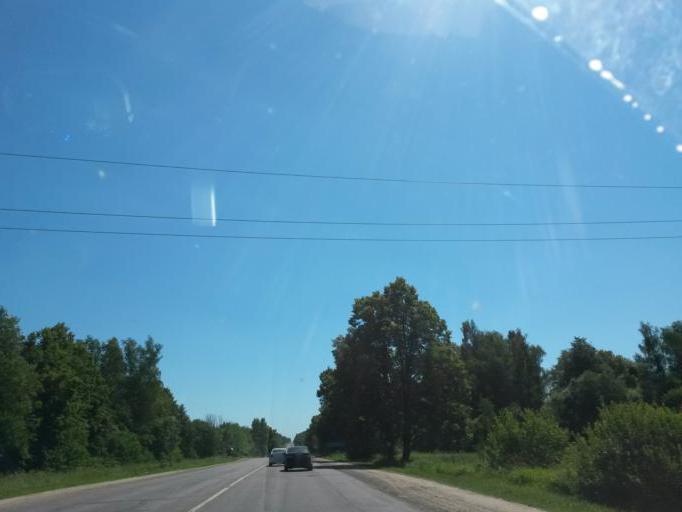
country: RU
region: Moskovskaya
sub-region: Chekhovskiy Rayon
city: Chekhov
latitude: 55.1040
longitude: 37.4454
